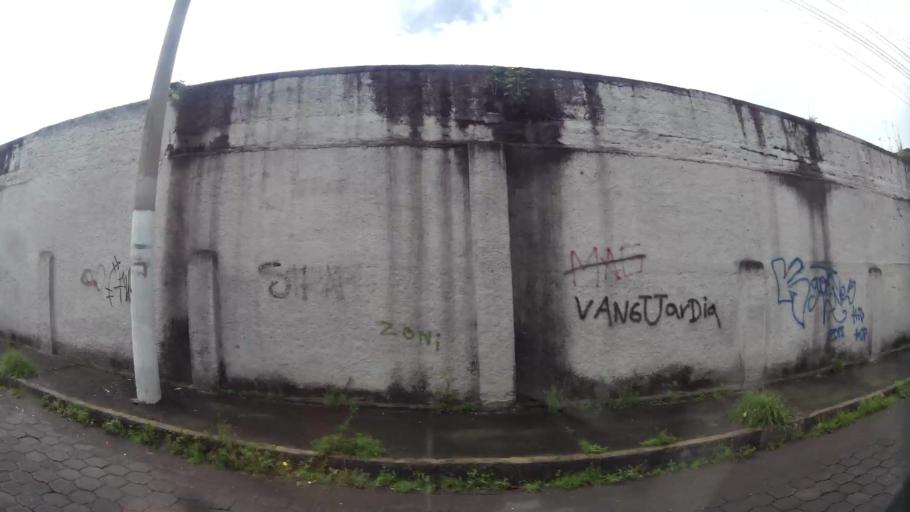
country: EC
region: Pichincha
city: Sangolqui
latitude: -0.2988
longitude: -78.4787
